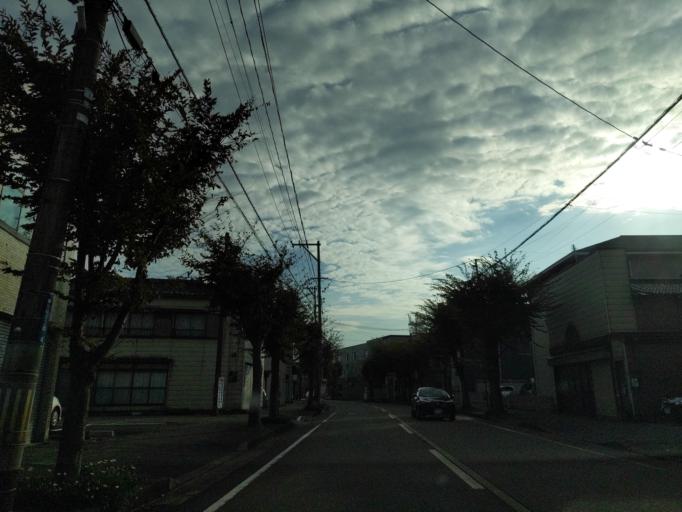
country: JP
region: Niigata
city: Kashiwazaki
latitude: 37.3712
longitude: 138.5607
